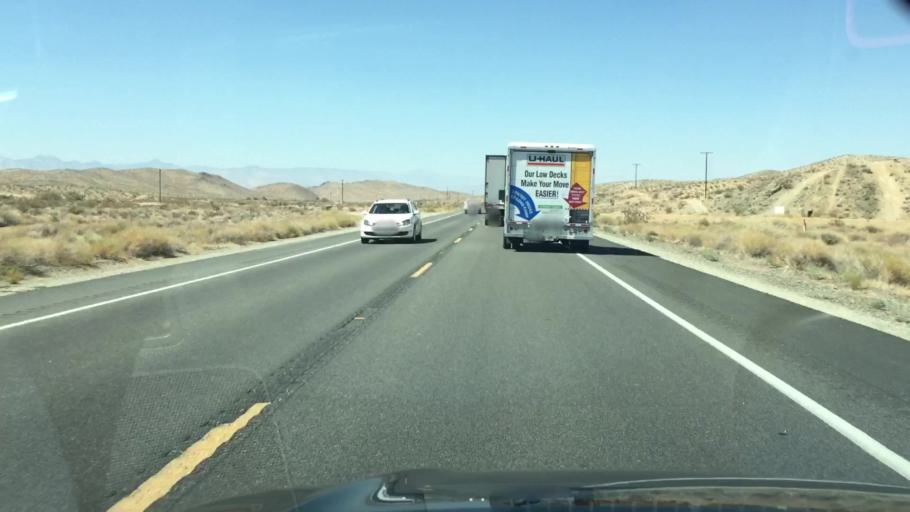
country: US
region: California
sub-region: Kern County
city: Ridgecrest
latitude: 35.5185
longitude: -117.6722
